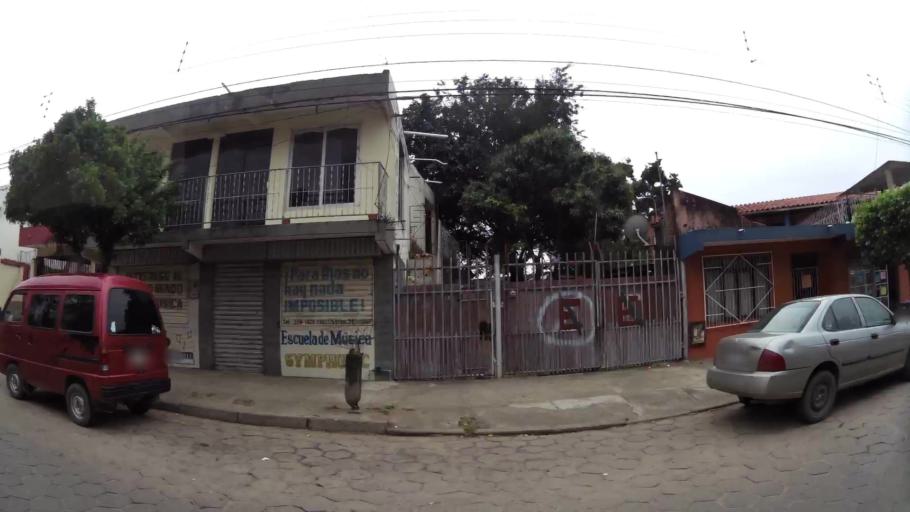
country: BO
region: Santa Cruz
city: Santa Cruz de la Sierra
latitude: -17.7987
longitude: -63.1904
